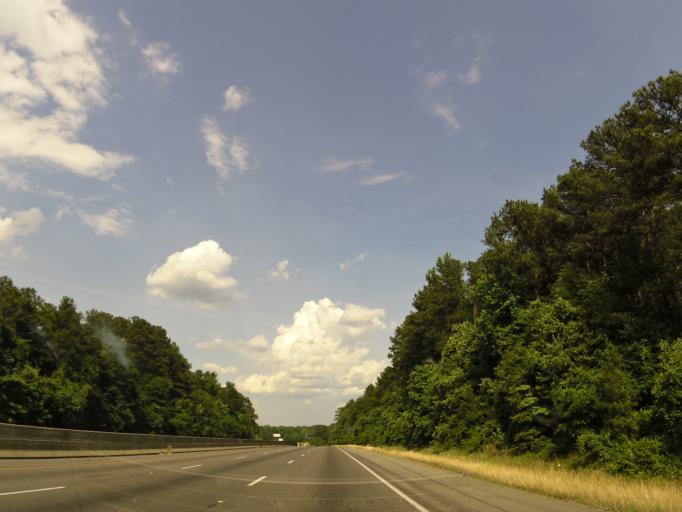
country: US
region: Alabama
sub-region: Tuscaloosa County
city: Coaling
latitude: 33.1770
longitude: -87.3841
